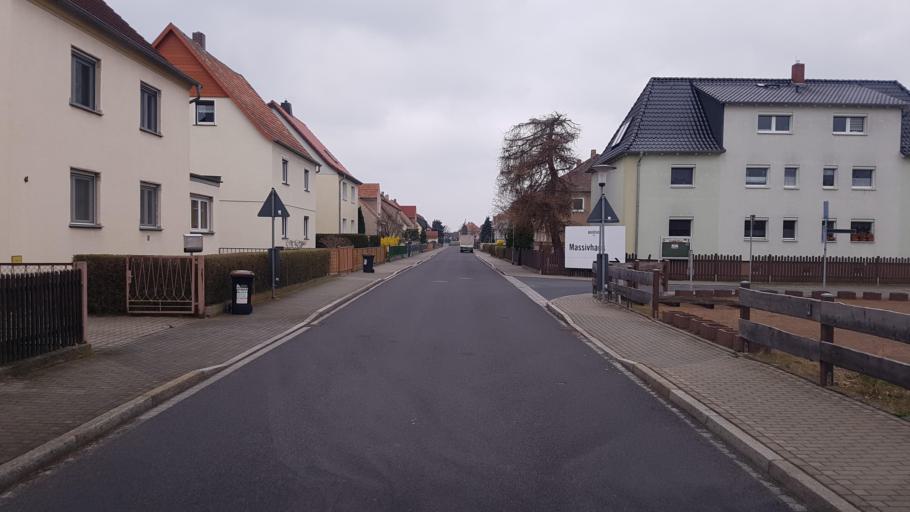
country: DE
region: Saxony
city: Nauwalde
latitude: 51.4183
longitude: 13.4468
